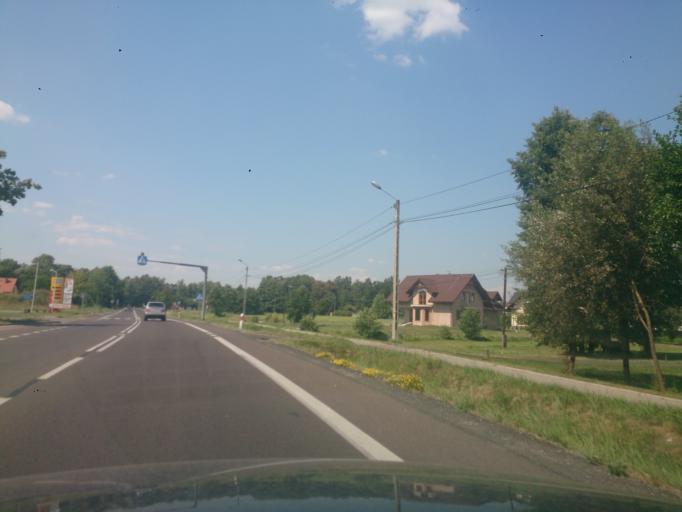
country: PL
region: Subcarpathian Voivodeship
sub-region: Powiat kolbuszowski
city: Dzikowiec
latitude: 50.2008
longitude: 21.8586
